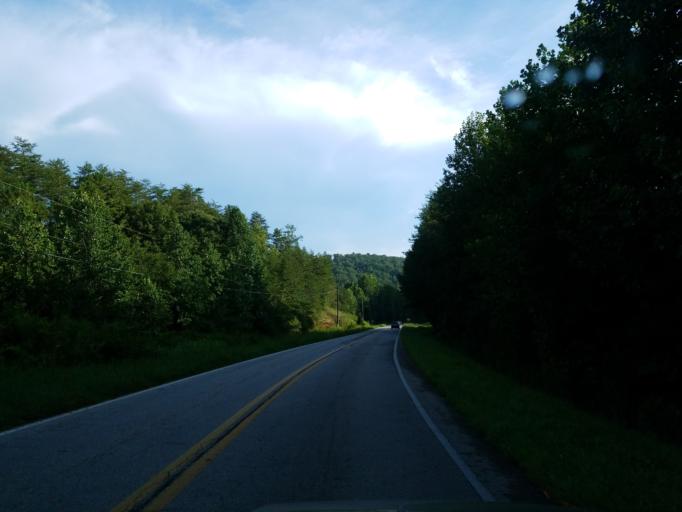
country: US
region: Georgia
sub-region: Lumpkin County
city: Dahlonega
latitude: 34.5511
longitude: -83.8833
